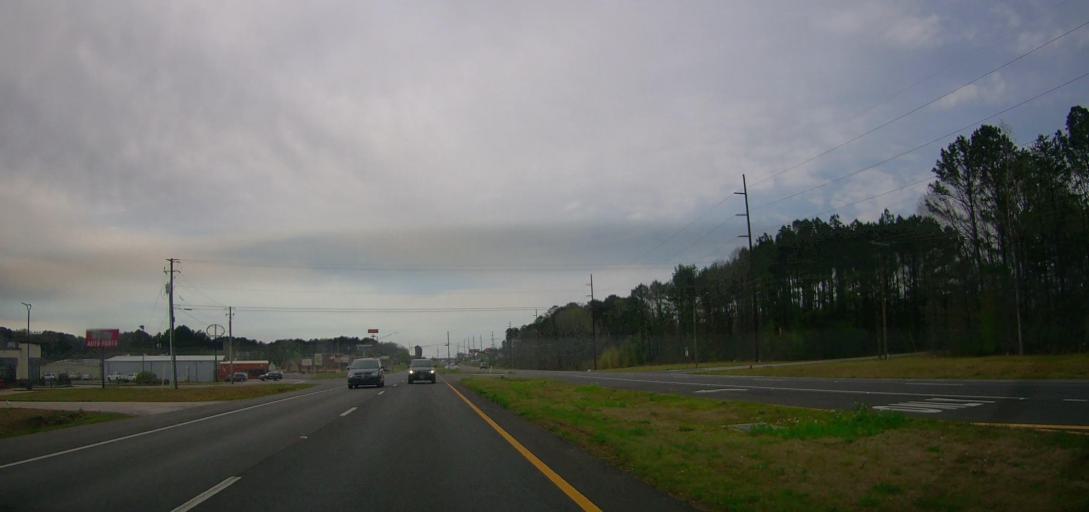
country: US
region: Alabama
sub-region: Walker County
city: Jasper
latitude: 33.8433
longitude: -87.2466
